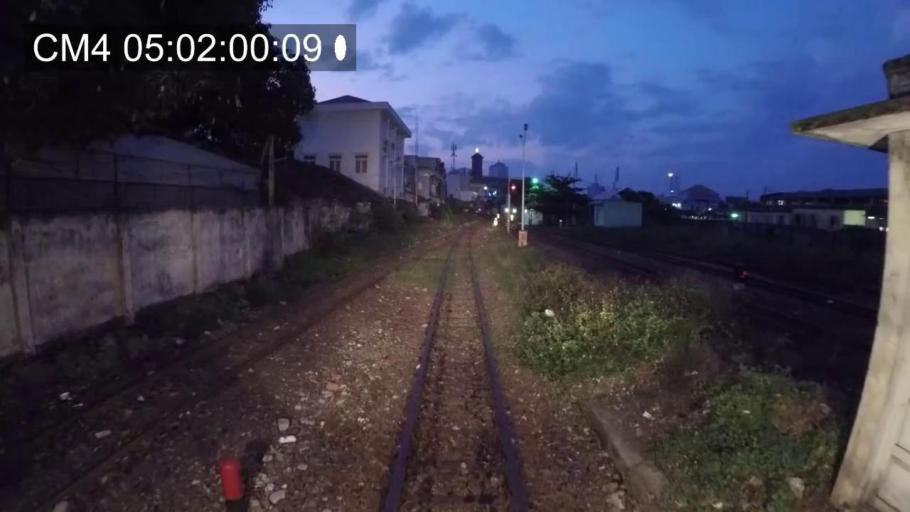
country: VN
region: Khanh Hoa
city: Nha Trang
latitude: 12.2498
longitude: 109.1794
